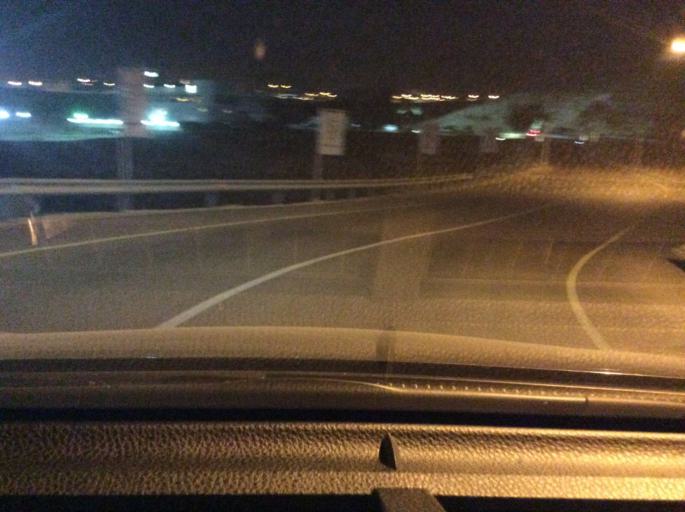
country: OM
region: Muhafazat Masqat
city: Bawshar
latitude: 23.5618
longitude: 58.3888
